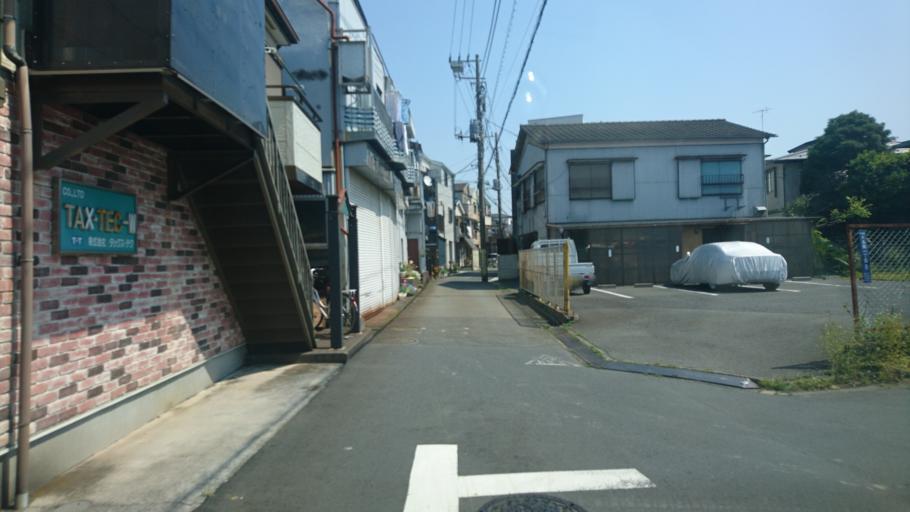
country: JP
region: Kanagawa
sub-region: Kawasaki-shi
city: Kawasaki
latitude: 35.5656
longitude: 139.7393
